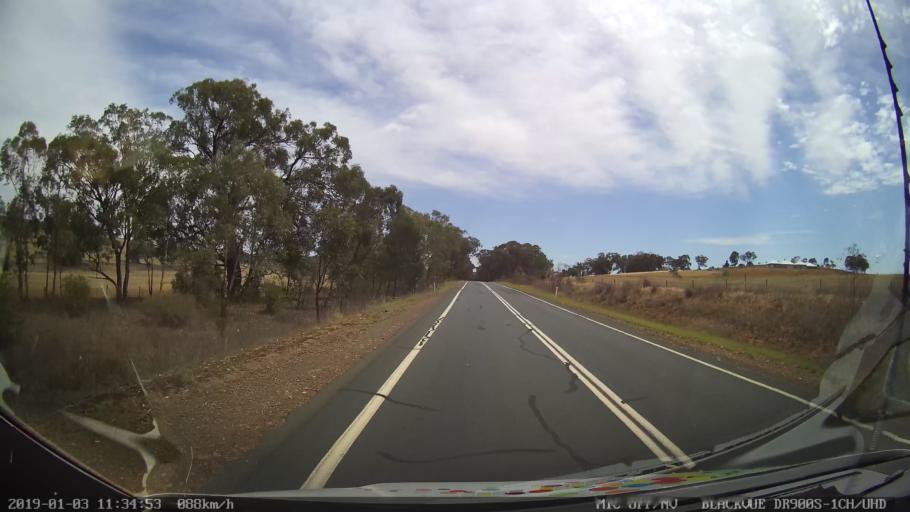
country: AU
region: New South Wales
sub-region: Weddin
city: Grenfell
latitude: -33.9290
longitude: 148.1602
